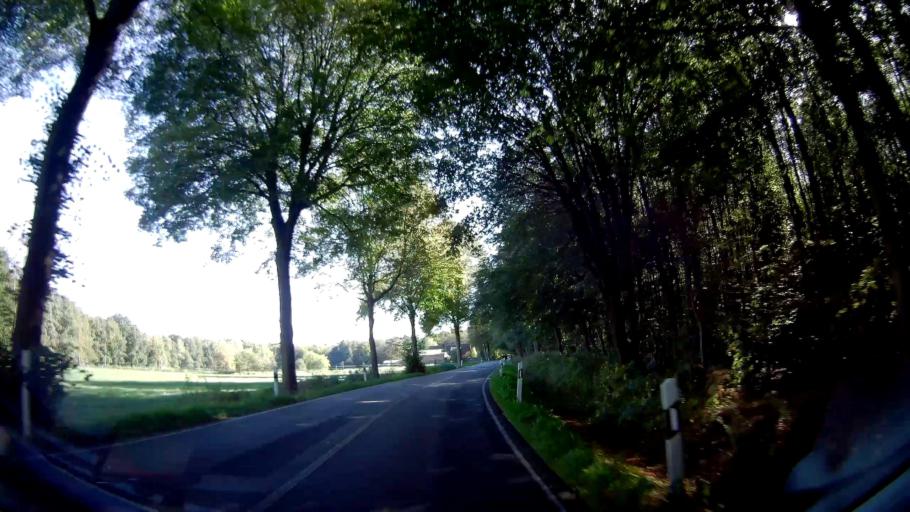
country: DE
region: North Rhine-Westphalia
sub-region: Regierungsbezirk Dusseldorf
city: Hunxe
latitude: 51.6123
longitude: 6.8154
